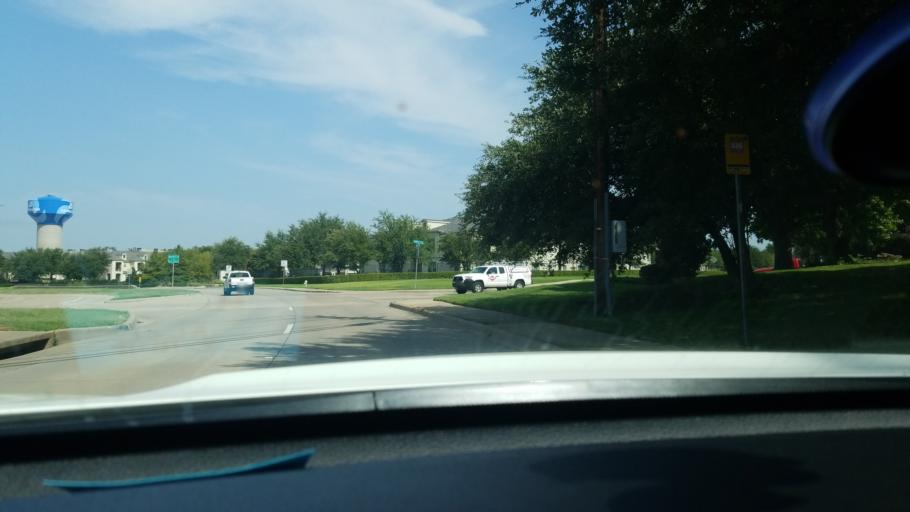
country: US
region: Texas
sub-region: Dallas County
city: Addison
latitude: 32.9704
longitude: -96.8514
